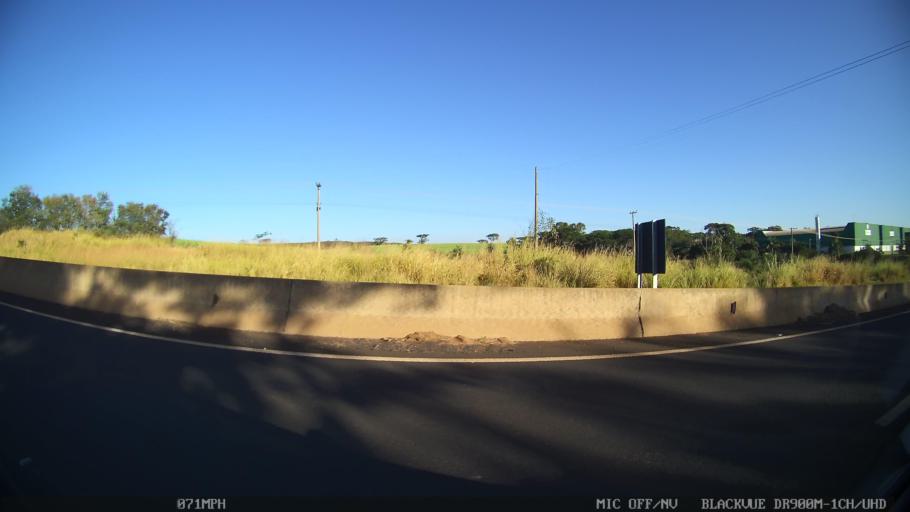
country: BR
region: Sao Paulo
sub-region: Guapiacu
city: Guapiacu
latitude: -20.7879
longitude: -49.2860
